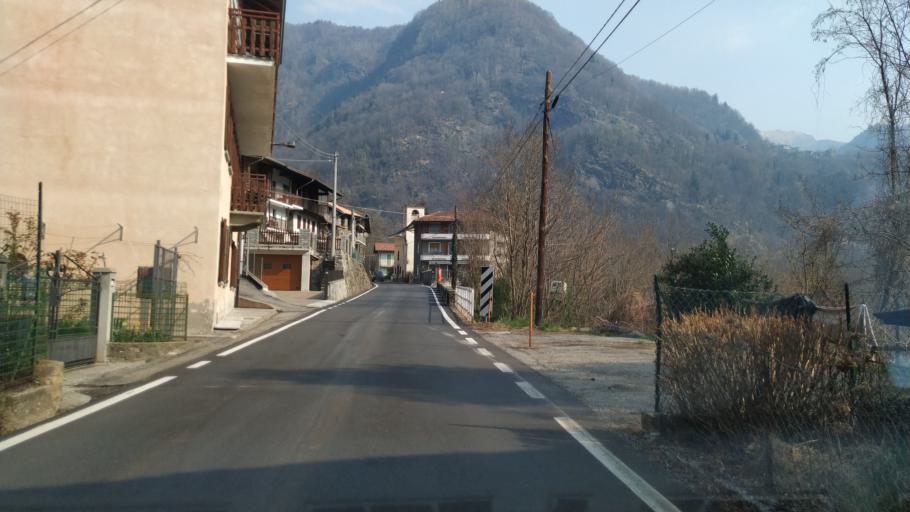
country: IT
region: Piedmont
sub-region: Provincia di Vercelli
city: Varallo
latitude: 45.8343
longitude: 8.2555
